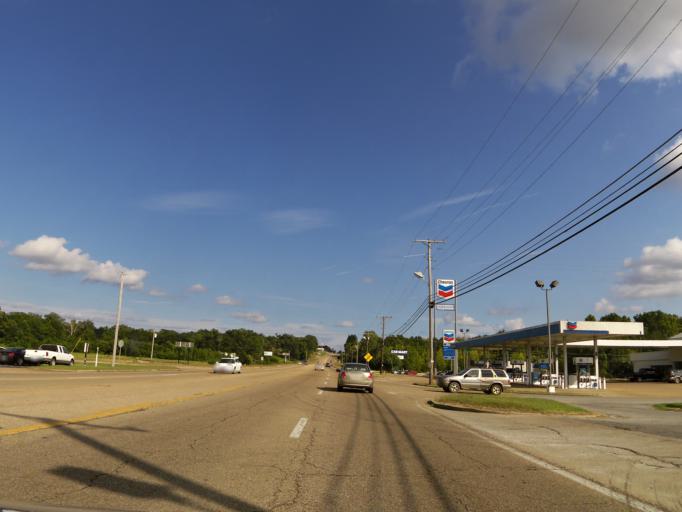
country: US
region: Mississippi
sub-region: Alcorn County
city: Corinth
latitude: 34.9128
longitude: -88.4991
